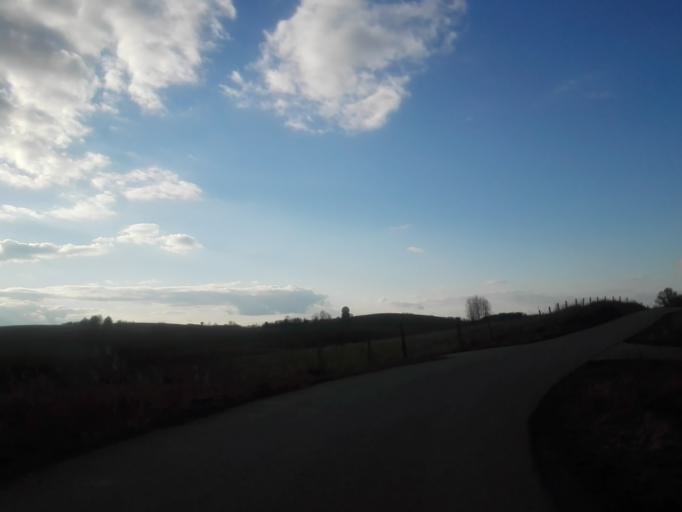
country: PL
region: Podlasie
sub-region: Suwalki
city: Suwalki
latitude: 54.2067
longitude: 23.0102
